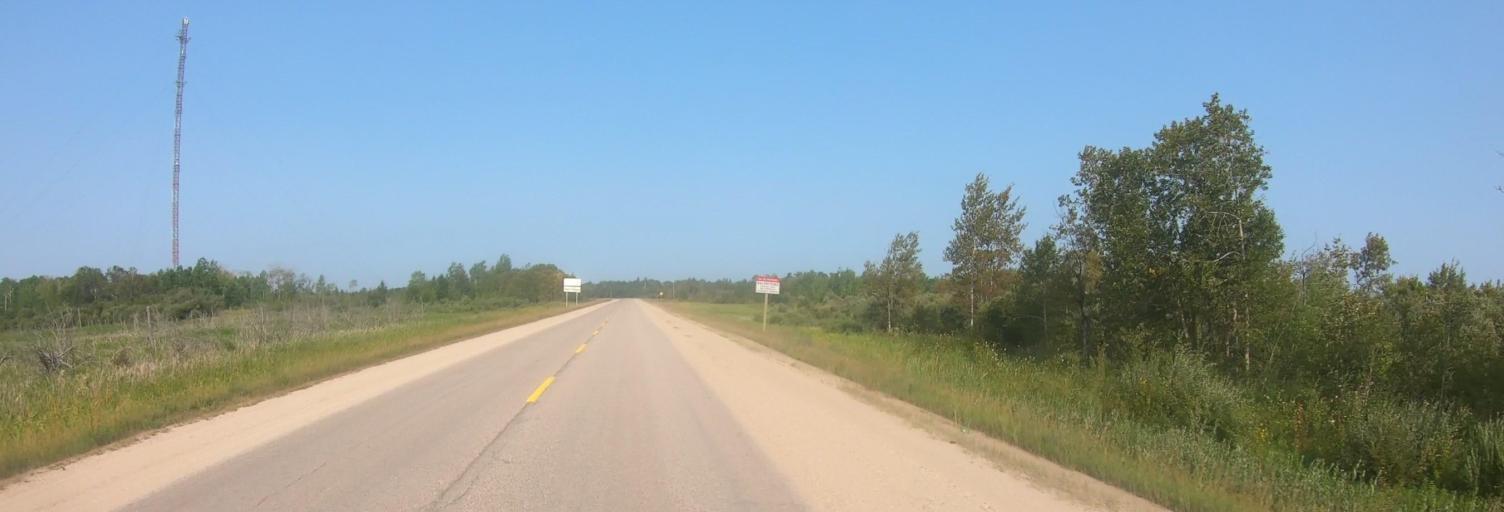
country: US
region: Minnesota
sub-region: Roseau County
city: Warroad
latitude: 49.0140
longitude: -95.4030
